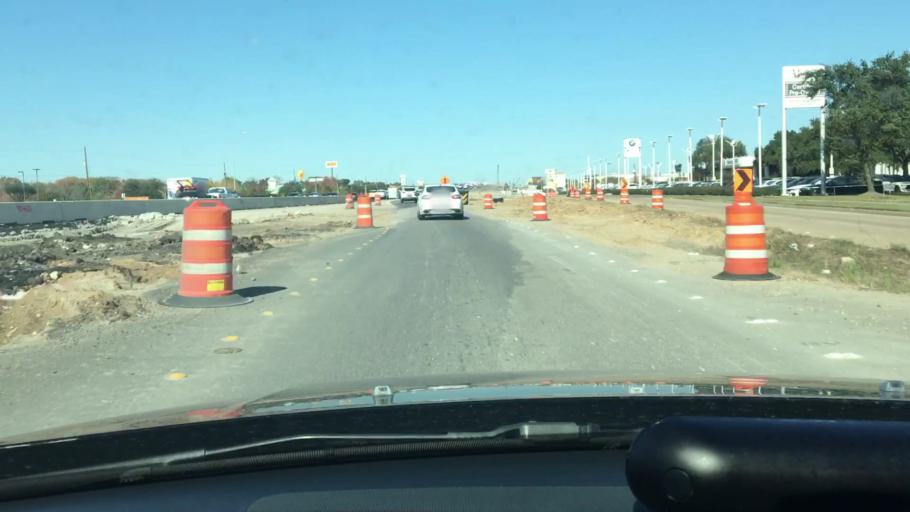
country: US
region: Texas
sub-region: Galveston County
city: League City
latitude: 29.4976
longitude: -95.1104
